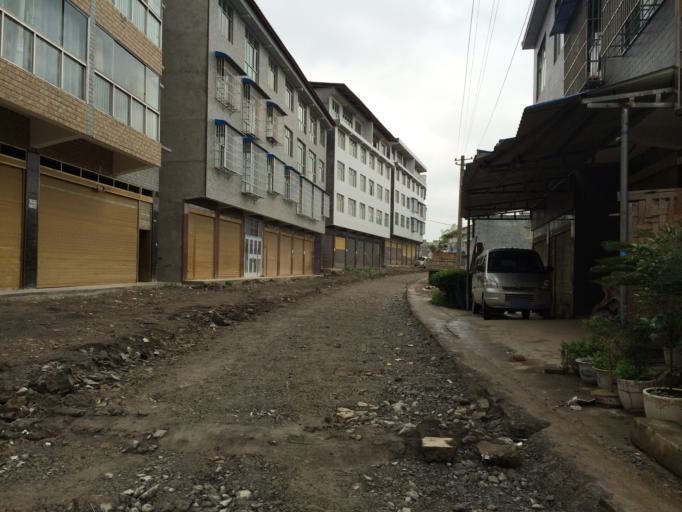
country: CN
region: Guizhou Sheng
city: Dalucao
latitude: 27.8311
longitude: 107.2530
